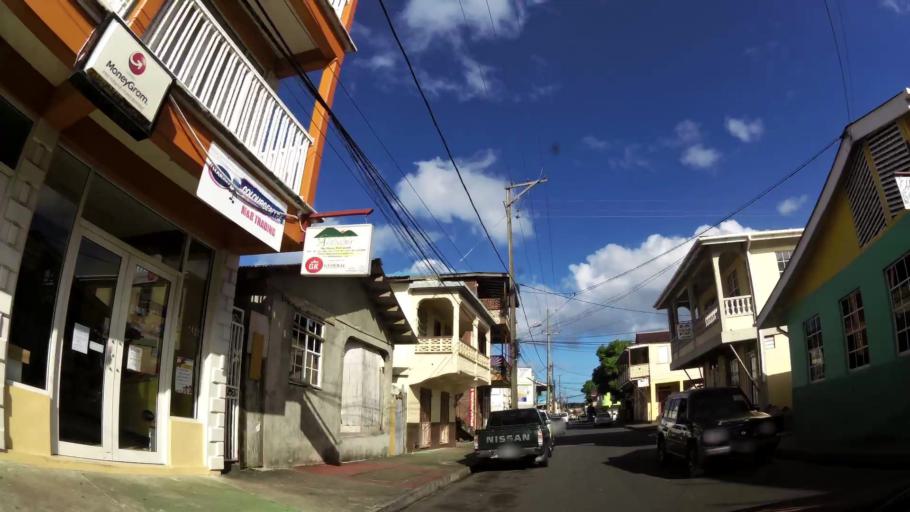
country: DM
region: Saint John
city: Portsmouth
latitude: 15.5754
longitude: -61.4567
